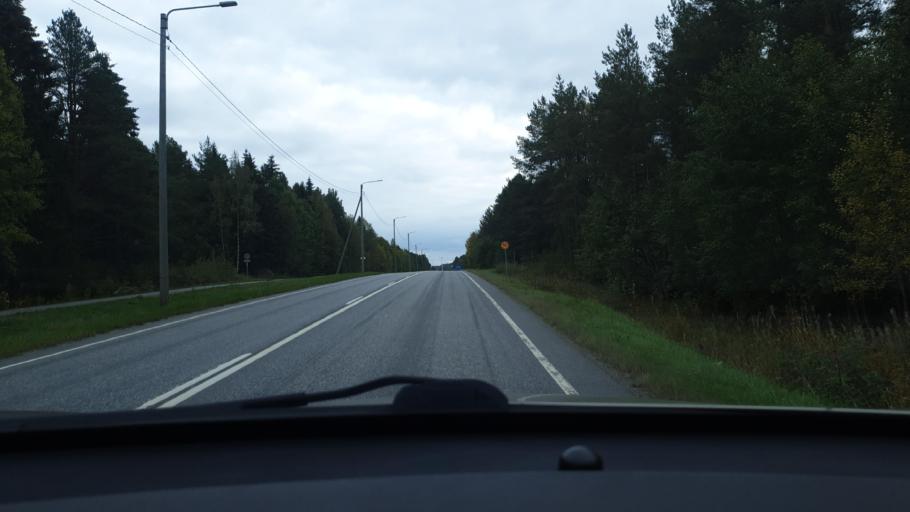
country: FI
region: Ostrobothnia
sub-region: Vaasa
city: Ristinummi
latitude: 63.0587
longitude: 21.7130
